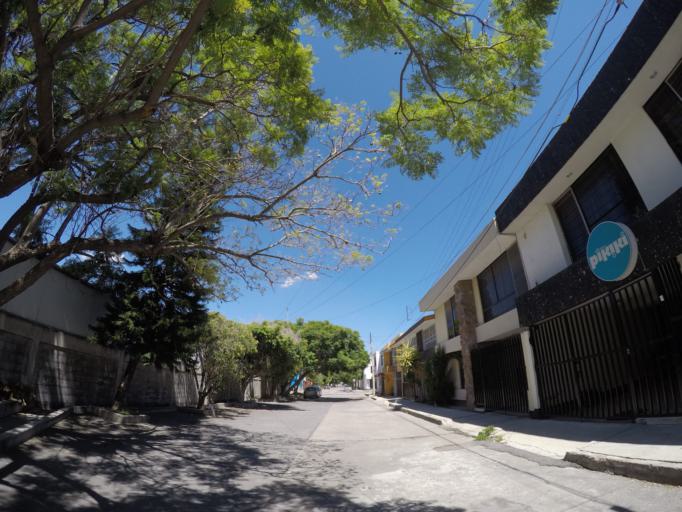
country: MX
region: San Luis Potosi
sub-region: San Luis Potosi
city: San Luis Potosi
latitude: 22.1462
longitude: -101.0130
